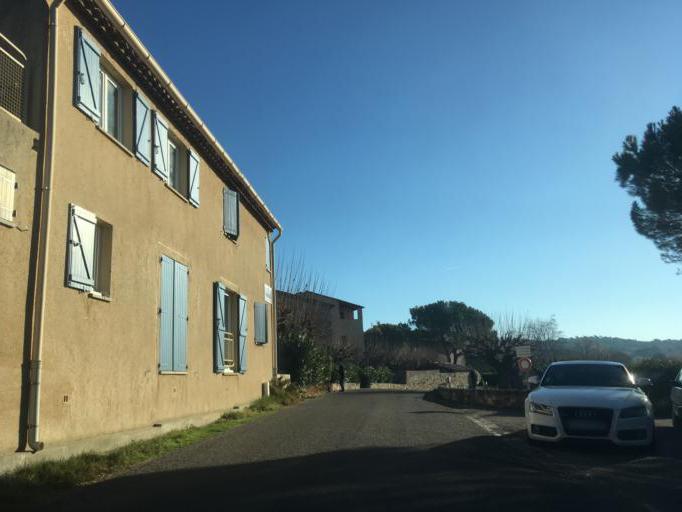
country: FR
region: Provence-Alpes-Cote d'Azur
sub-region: Departement du Var
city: Villecroze
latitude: 43.5812
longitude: 6.2744
